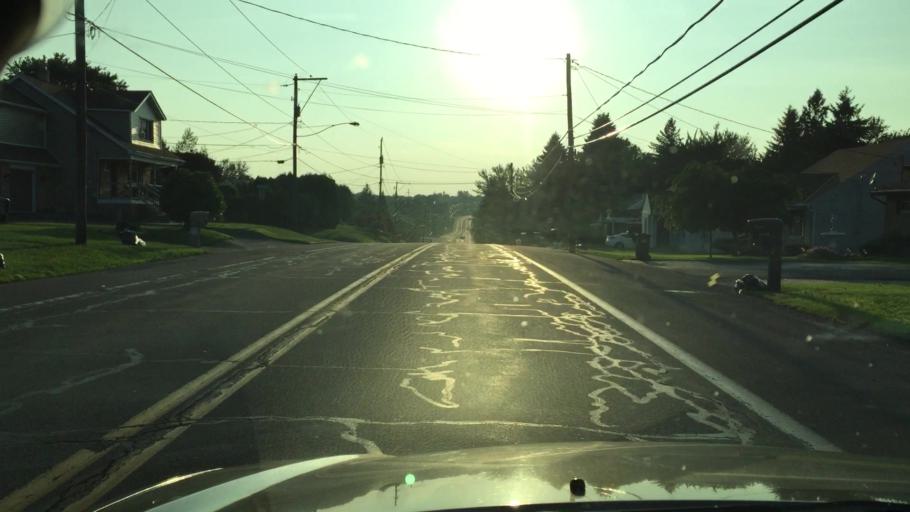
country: US
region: Pennsylvania
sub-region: Luzerne County
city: Hazleton
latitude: 40.9392
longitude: -75.9406
